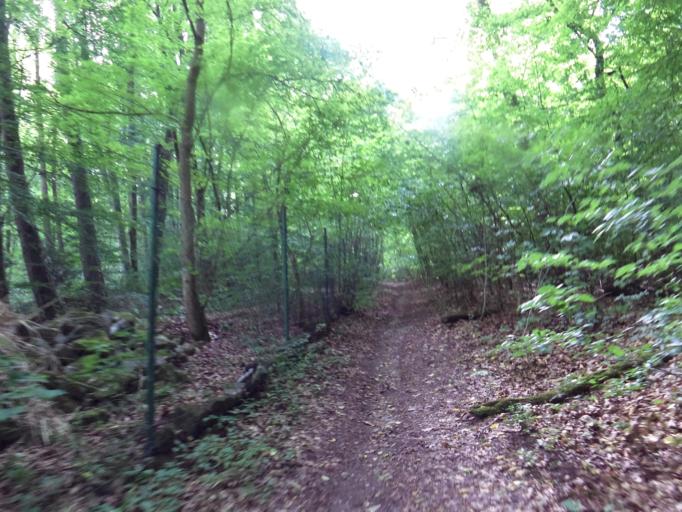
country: DE
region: Bavaria
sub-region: Regierungsbezirk Unterfranken
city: Wuerzburg
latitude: 49.7657
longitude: 9.9112
